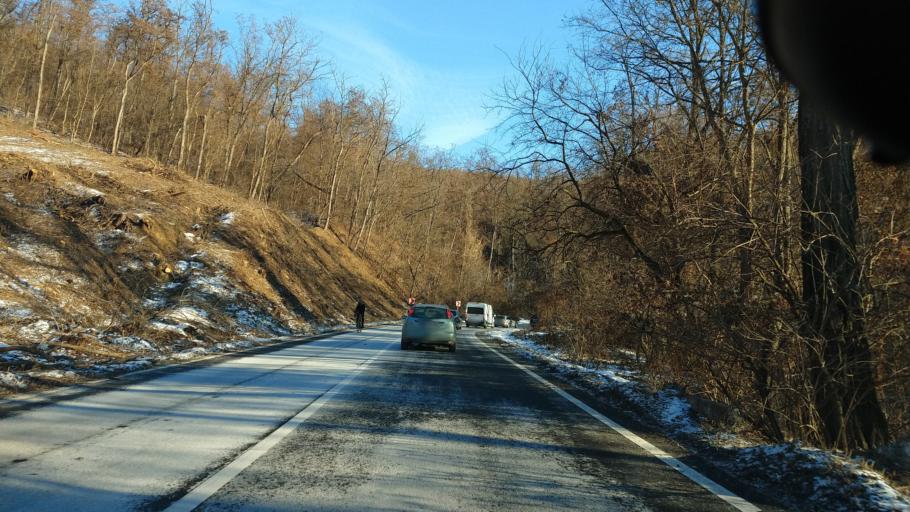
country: RO
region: Bacau
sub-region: Comuna Luizi-Calugara
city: Luizi-Calugara
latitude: 46.5428
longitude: 26.8199
